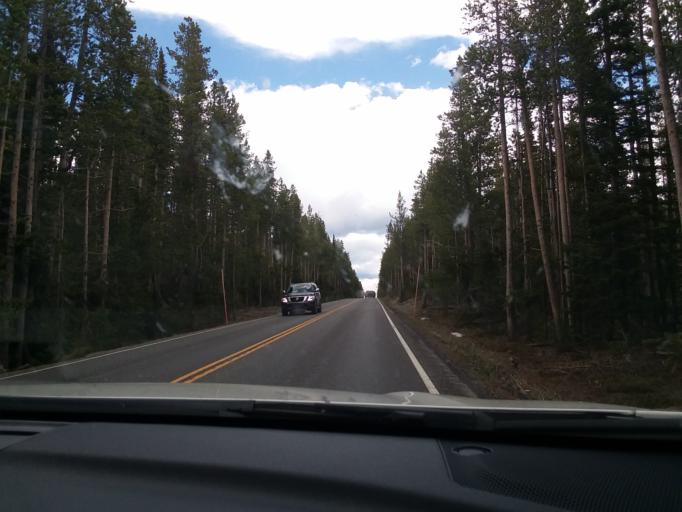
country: US
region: Idaho
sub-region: Teton County
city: Driggs
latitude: 44.1718
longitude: -110.6627
